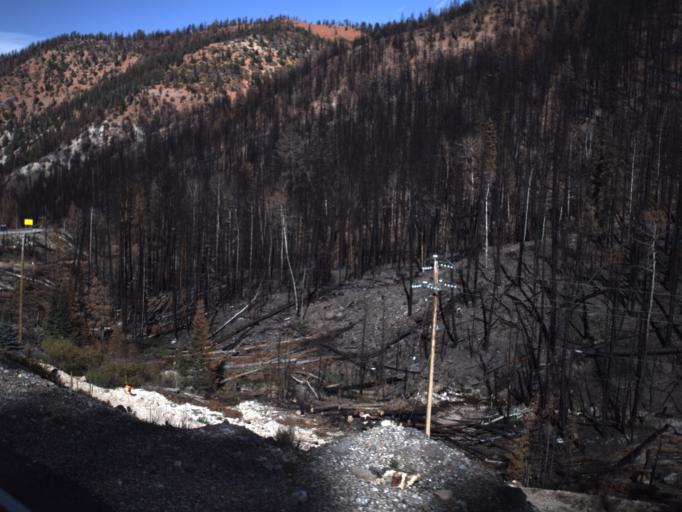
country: US
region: Utah
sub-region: Iron County
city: Parowan
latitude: 37.7244
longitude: -112.8422
